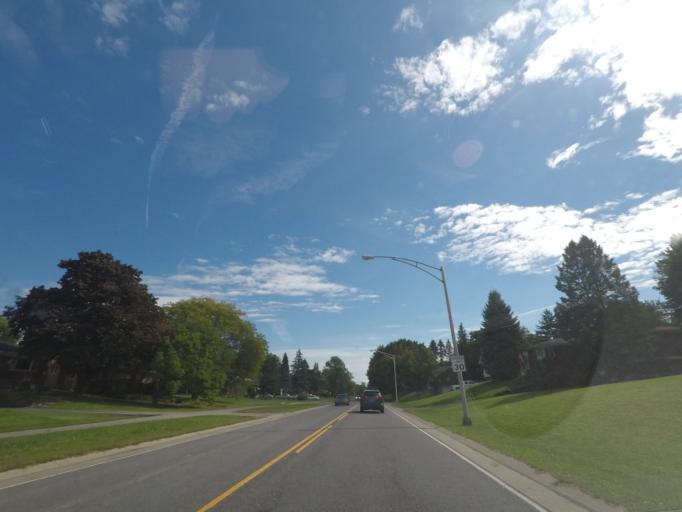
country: US
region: New York
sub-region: Albany County
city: Albany
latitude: 42.6481
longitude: -73.7940
